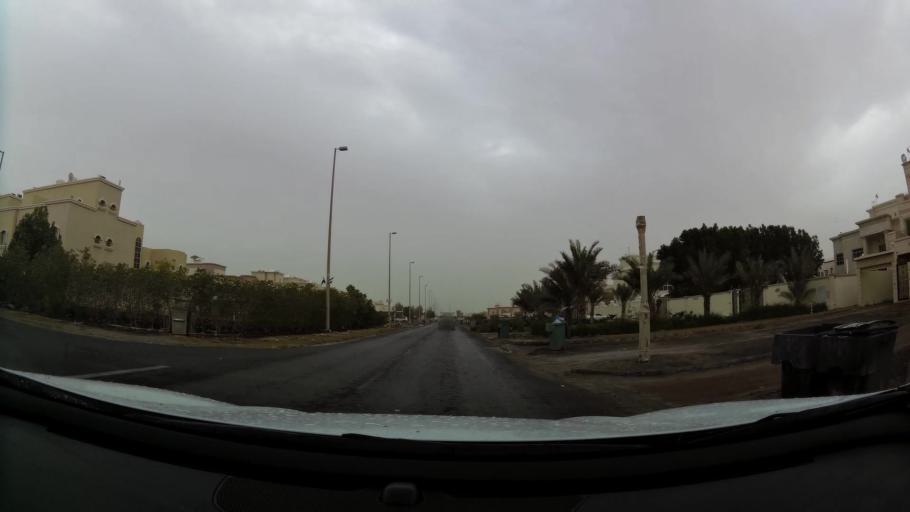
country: AE
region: Abu Dhabi
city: Abu Dhabi
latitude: 24.4147
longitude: 54.5855
